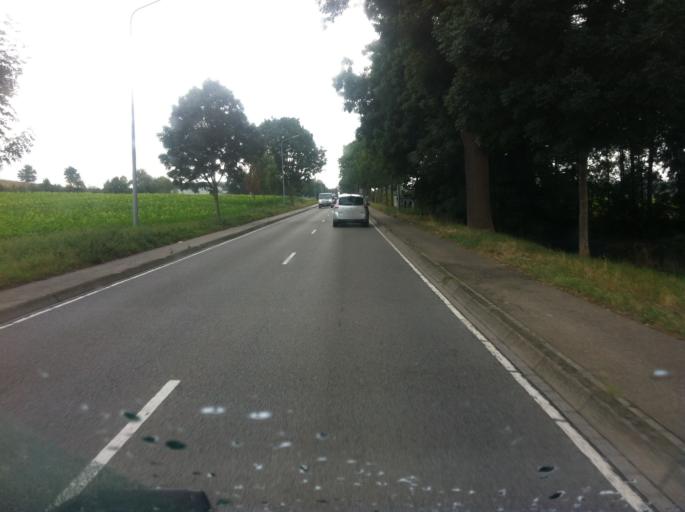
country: NL
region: Limburg
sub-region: Gemeente Maastricht
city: Maastricht
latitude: 50.8722
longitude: 5.6726
